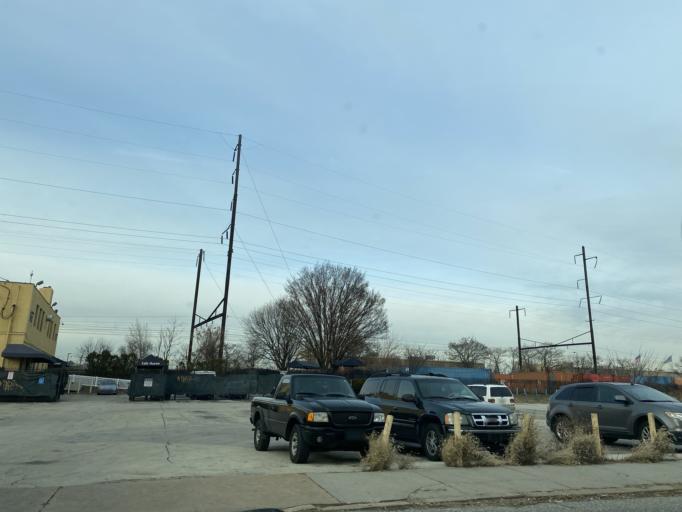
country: US
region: New Jersey
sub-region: Burlington County
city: Palmyra
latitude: 40.0101
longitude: -75.0687
